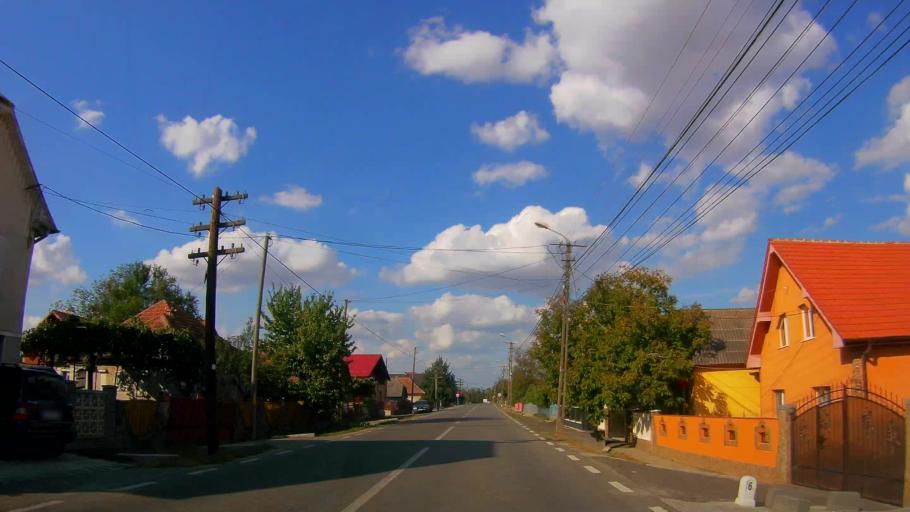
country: RO
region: Satu Mare
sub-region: Comuna Turulung
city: Draguseni
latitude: 47.9070
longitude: 23.0765
